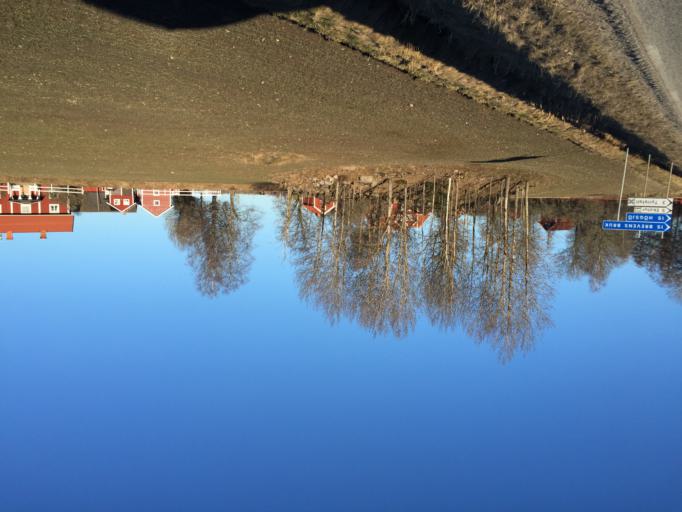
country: SE
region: OEstergoetland
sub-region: Finspangs Kommun
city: Finspang
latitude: 58.8974
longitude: 15.6909
